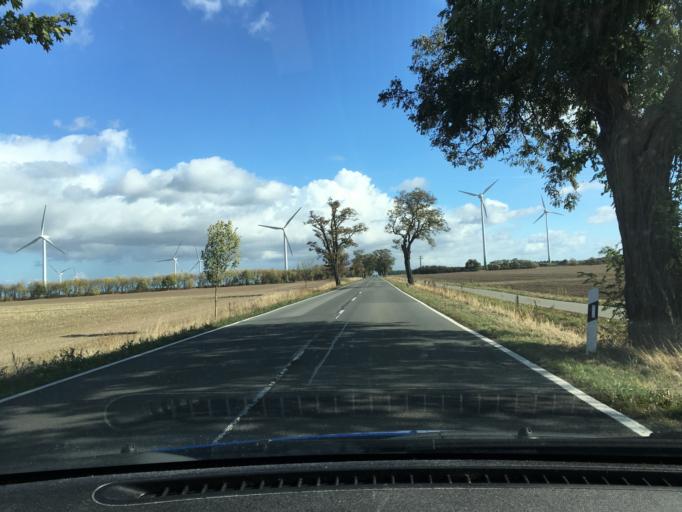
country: DE
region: Saxony-Anhalt
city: Pretzier
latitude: 52.8397
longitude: 11.2171
